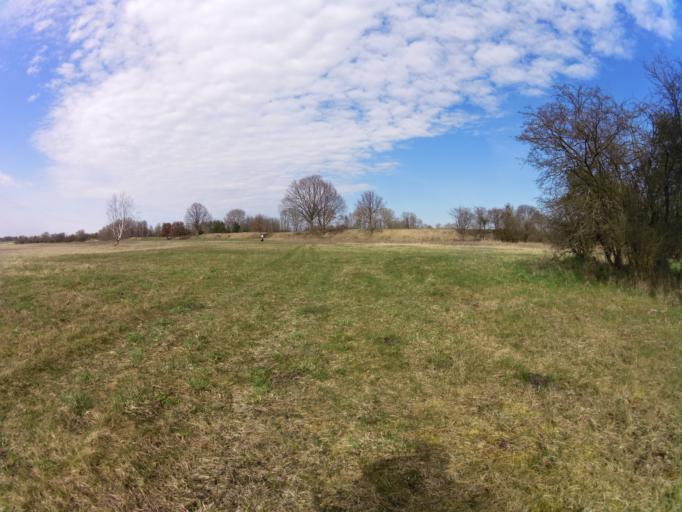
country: PL
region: West Pomeranian Voivodeship
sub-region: Powiat mysliborski
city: Mysliborz
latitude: 52.9697
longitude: 14.8815
